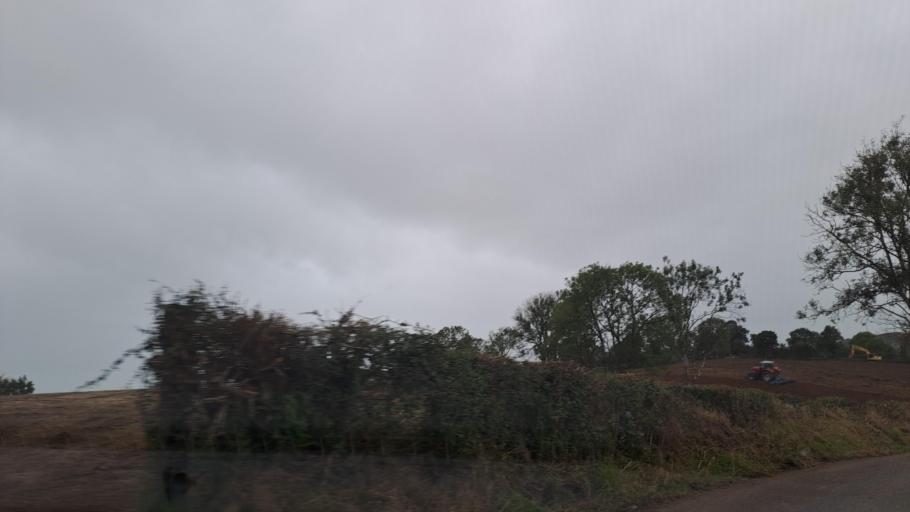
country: IE
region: Ulster
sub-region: An Cabhan
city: Kingscourt
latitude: 53.9992
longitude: -6.8543
